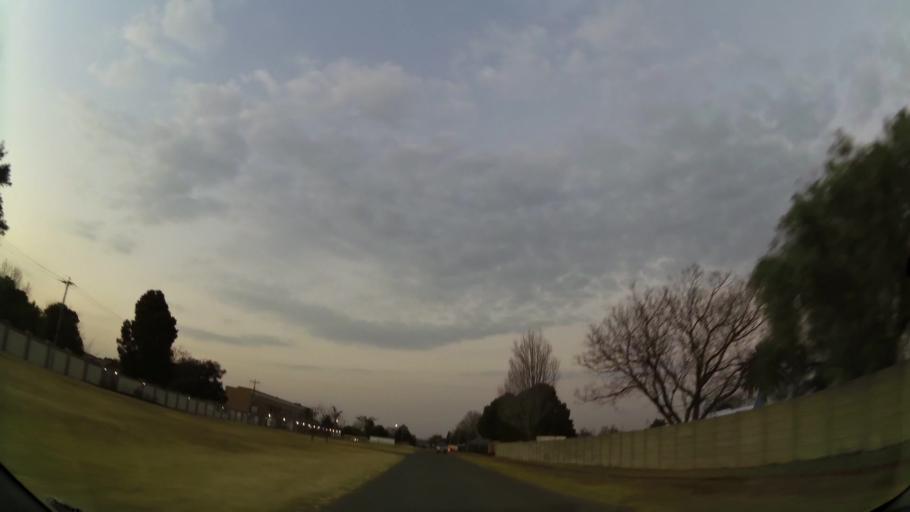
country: ZA
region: Gauteng
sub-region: Ekurhuleni Metropolitan Municipality
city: Benoni
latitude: -26.1402
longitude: 28.3124
